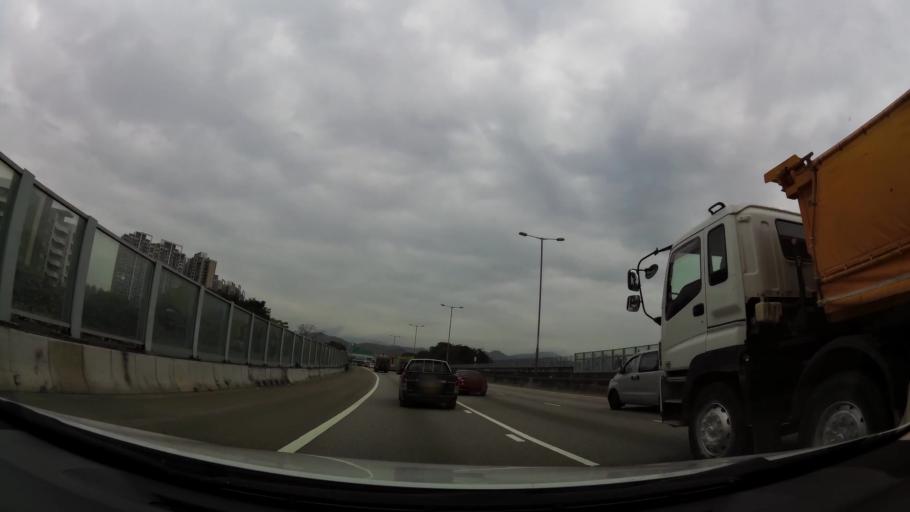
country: HK
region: Yuen Long
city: Yuen Long Kau Hui
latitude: 22.4362
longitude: 114.0190
